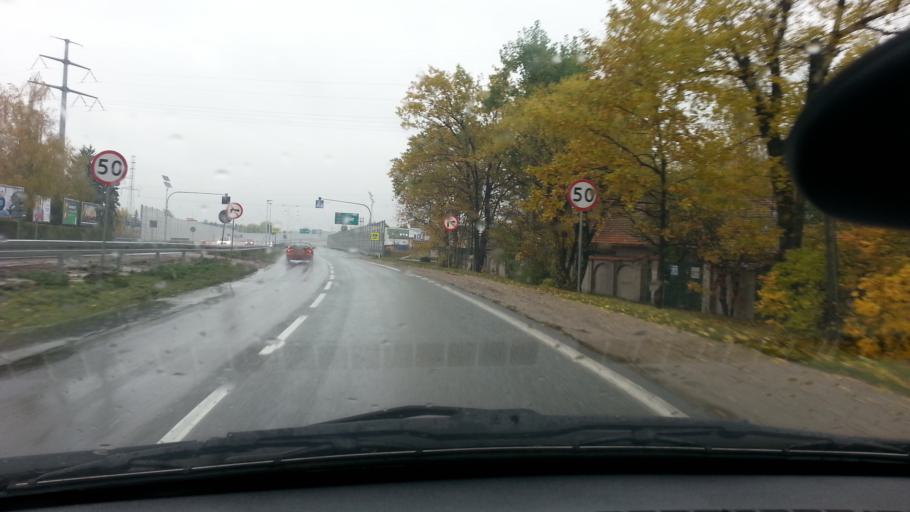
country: PL
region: Masovian Voivodeship
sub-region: Powiat pruszkowski
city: Michalowice
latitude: 52.1775
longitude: 20.8720
